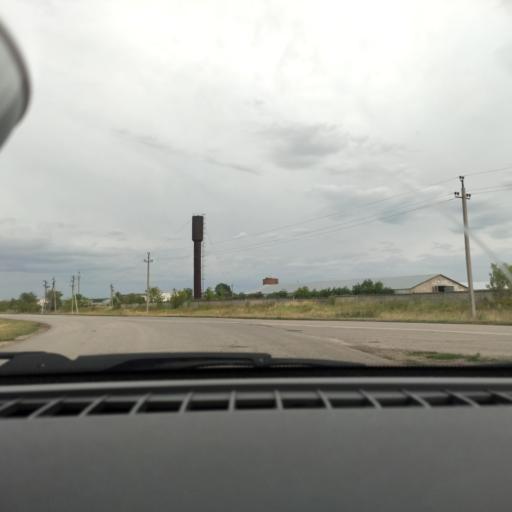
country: RU
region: Samara
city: Georgiyevka
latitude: 53.4729
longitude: 50.9347
